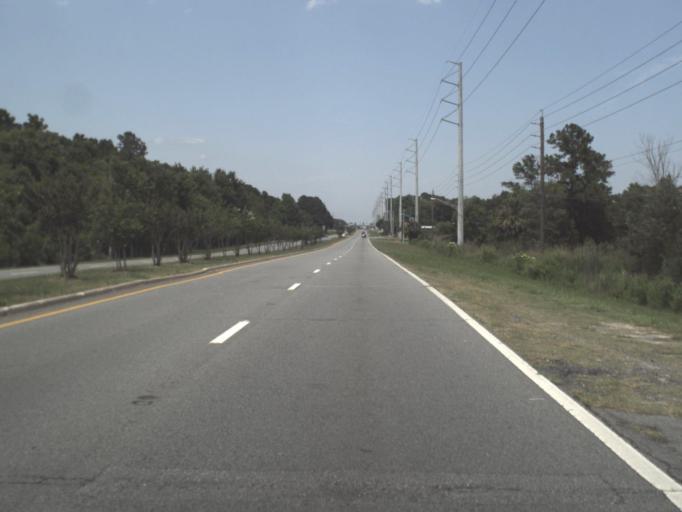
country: US
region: Florida
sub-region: Duval County
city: Jacksonville
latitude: 30.4377
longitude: -81.6423
